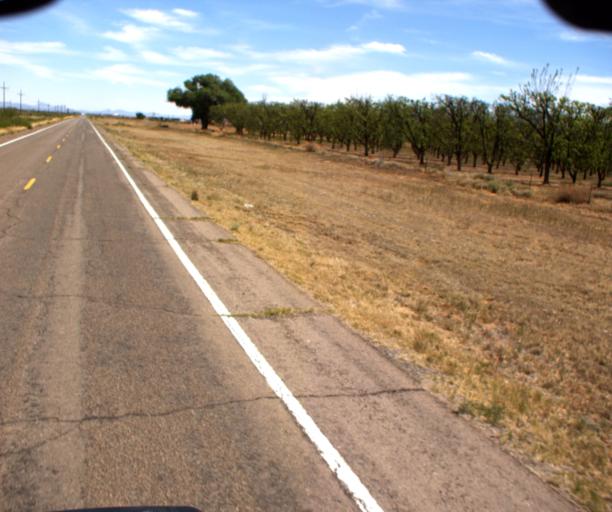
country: US
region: Arizona
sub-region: Cochise County
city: Willcox
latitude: 32.3237
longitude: -109.4674
